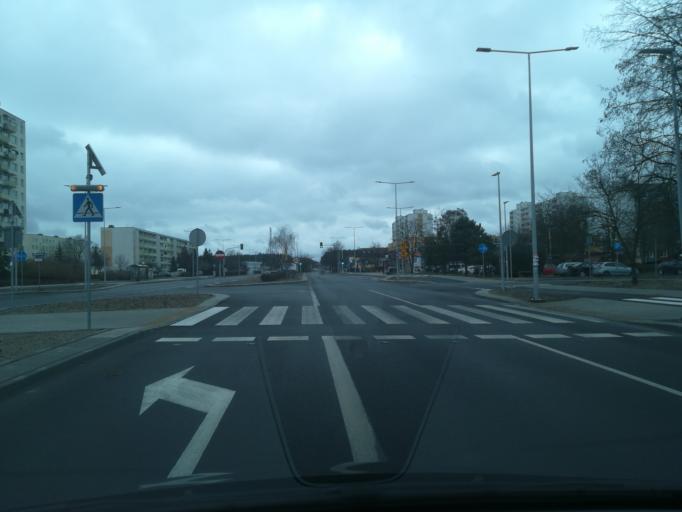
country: PL
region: Kujawsko-Pomorskie
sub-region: Powiat torunski
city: Lubicz Dolny
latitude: 53.0264
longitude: 18.6872
